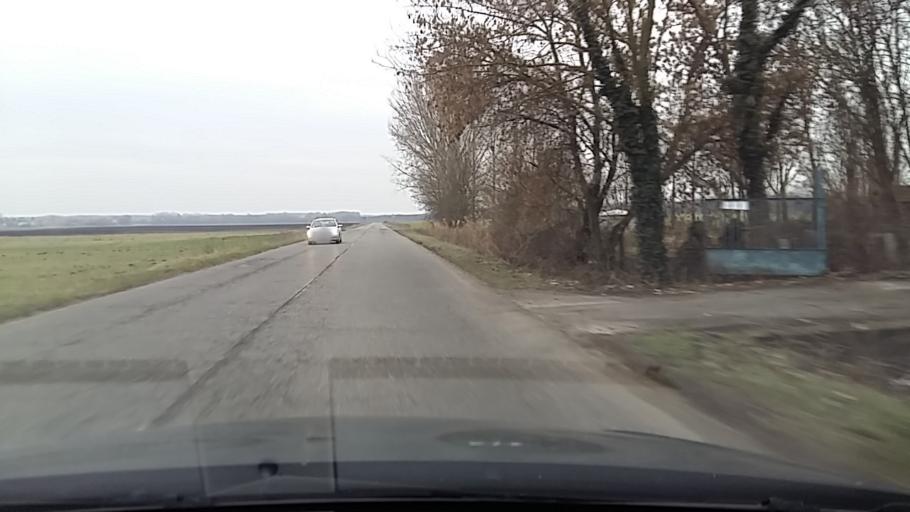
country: HU
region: Szabolcs-Szatmar-Bereg
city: Nyirbogdany
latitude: 48.0599
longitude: 21.8597
